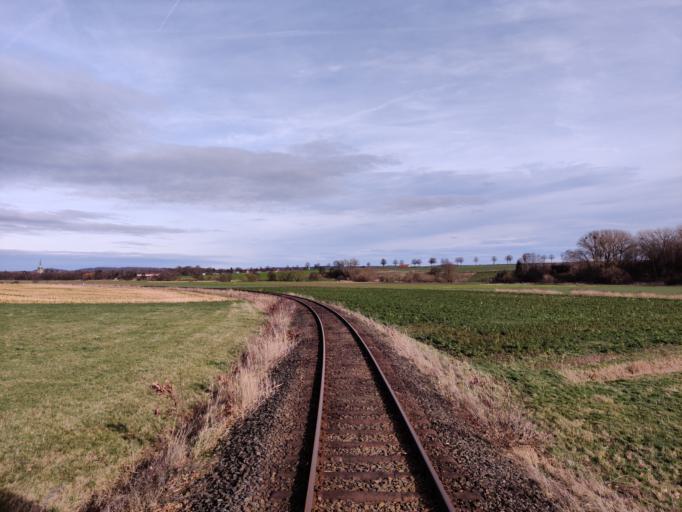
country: DE
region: Lower Saxony
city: Bockenem
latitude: 51.9929
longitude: 10.1212
